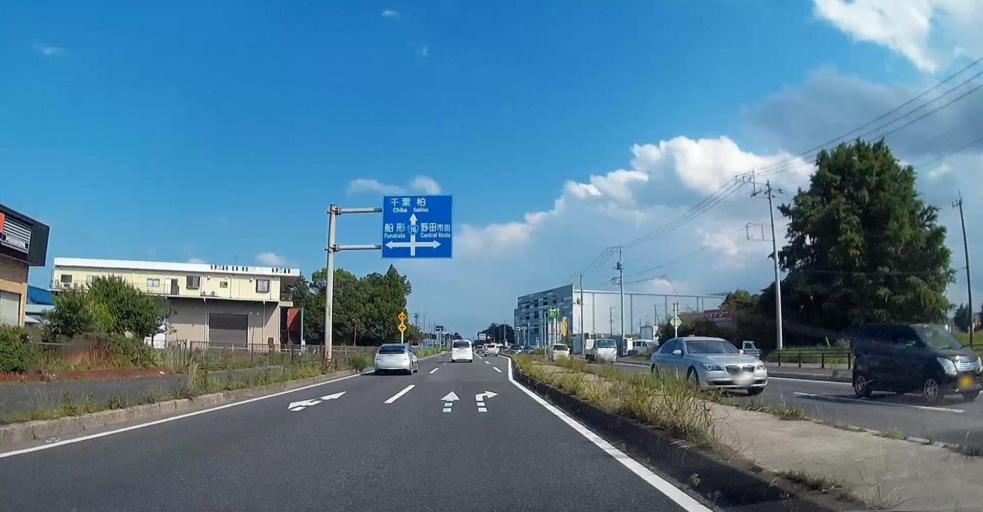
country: JP
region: Chiba
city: Noda
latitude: 35.9920
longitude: 139.8502
